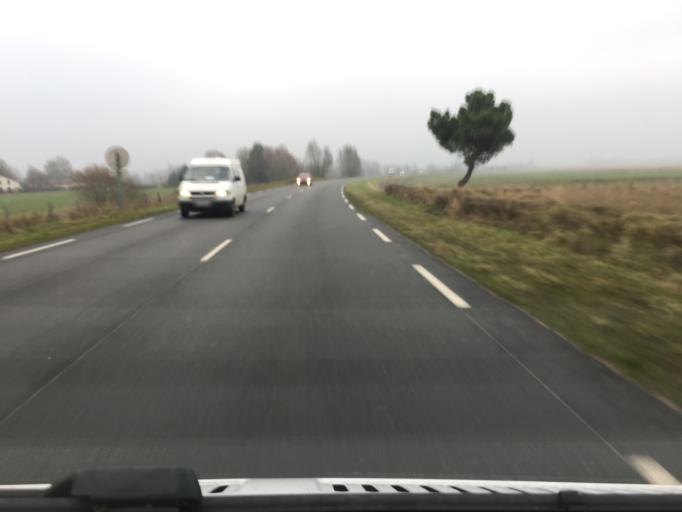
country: FR
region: Picardie
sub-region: Departement de la Somme
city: Saint-Valery-sur-Somme
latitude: 50.2101
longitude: 1.6758
